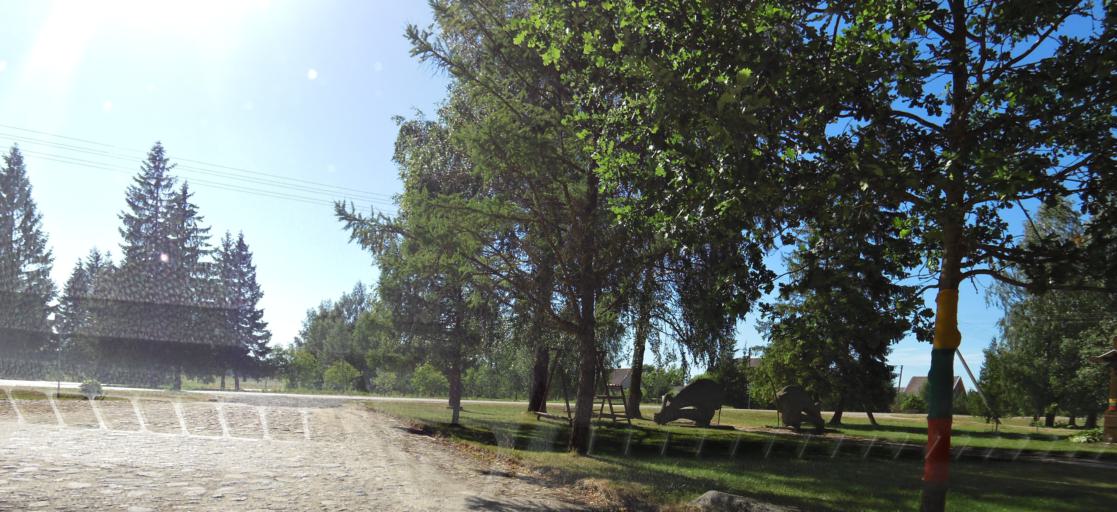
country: LT
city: Vabalninkas
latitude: 56.0268
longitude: 24.6601
